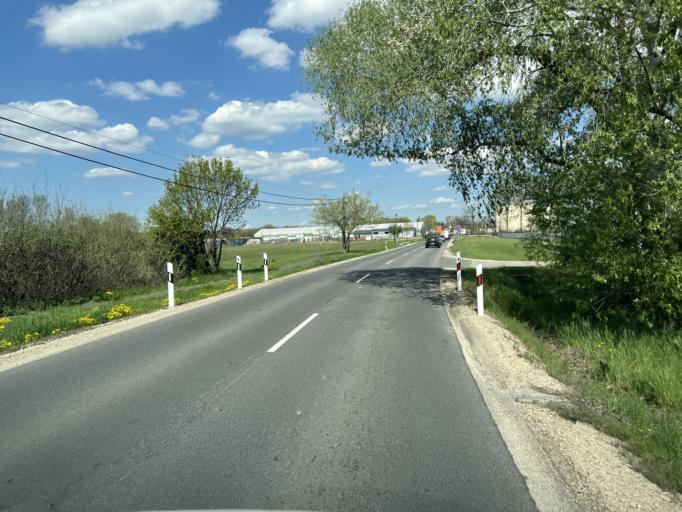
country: HU
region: Pest
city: Gyal
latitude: 47.3687
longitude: 19.2118
